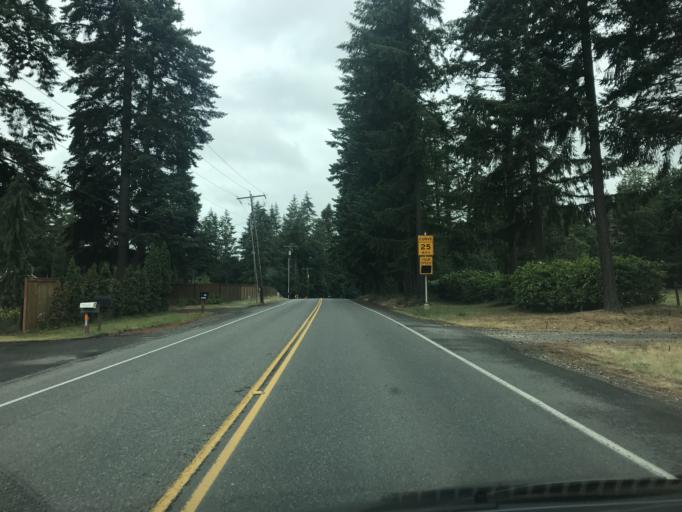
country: US
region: Washington
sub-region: King County
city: Lake Morton-Berrydale
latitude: 47.3420
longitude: -122.0966
